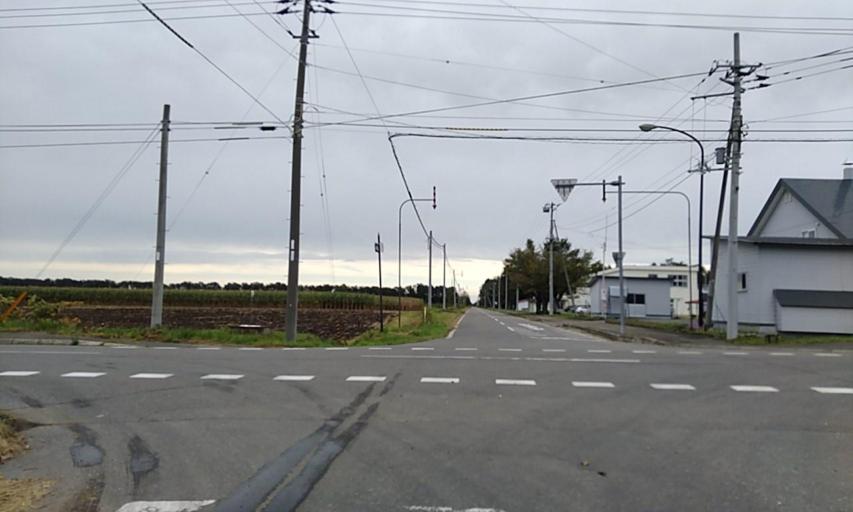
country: JP
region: Hokkaido
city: Obihiro
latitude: 42.6400
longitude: 143.0941
